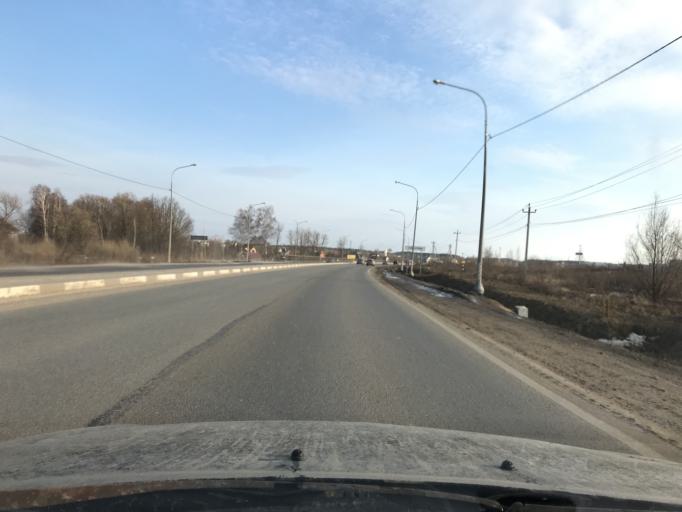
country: RU
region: Kaluga
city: Kaluga
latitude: 54.4785
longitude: 36.2348
